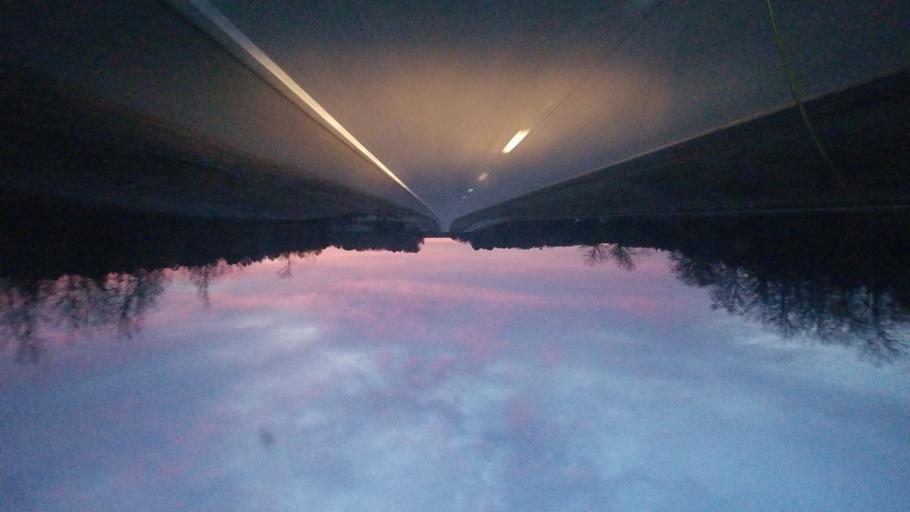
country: US
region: Missouri
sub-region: Shannon County
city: Winona
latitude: 36.9981
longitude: -91.4370
